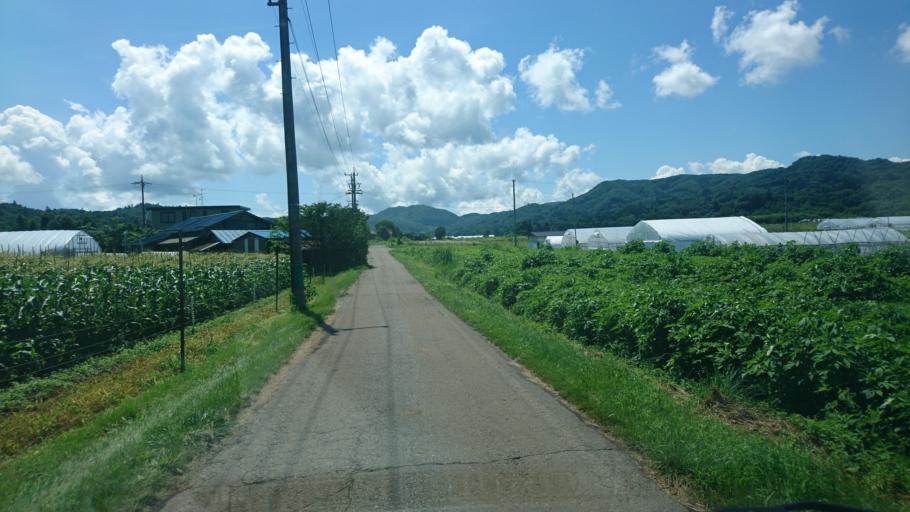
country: JP
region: Nagano
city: Saku
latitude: 36.3171
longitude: 138.5850
